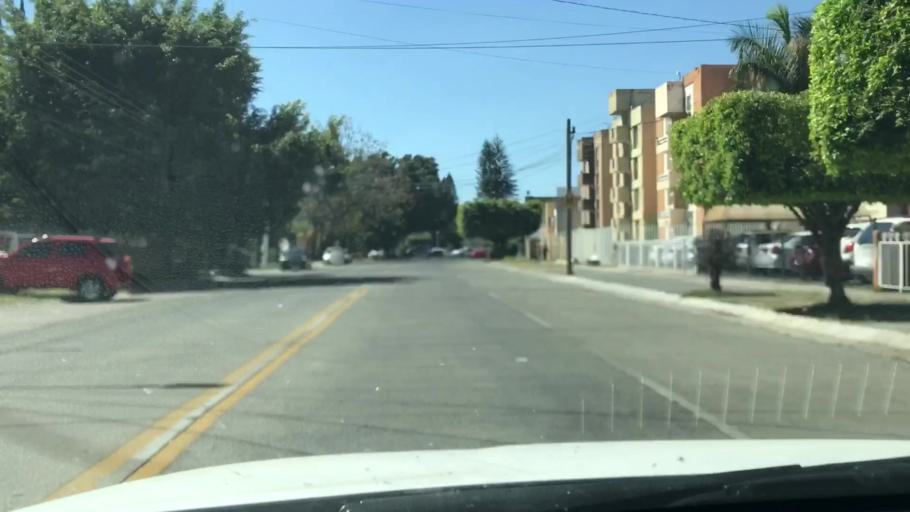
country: MX
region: Jalisco
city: Guadalajara
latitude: 20.6328
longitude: -103.4293
